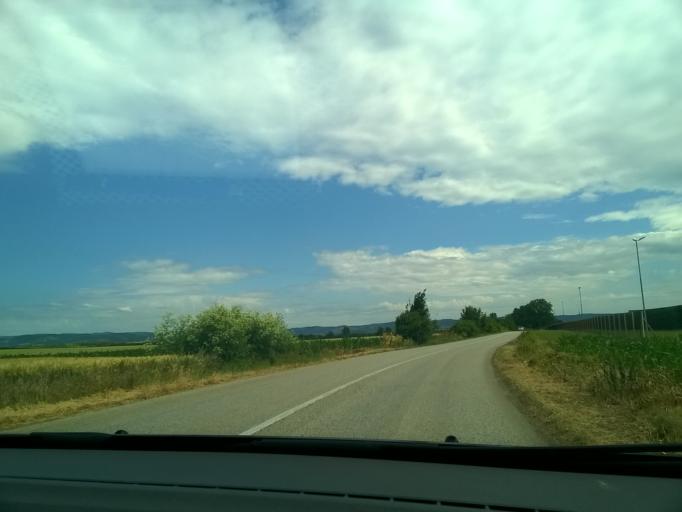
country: RS
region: Autonomna Pokrajina Vojvodina
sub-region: Sremski Okrug
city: Ruma
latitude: 45.0436
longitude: 19.8044
